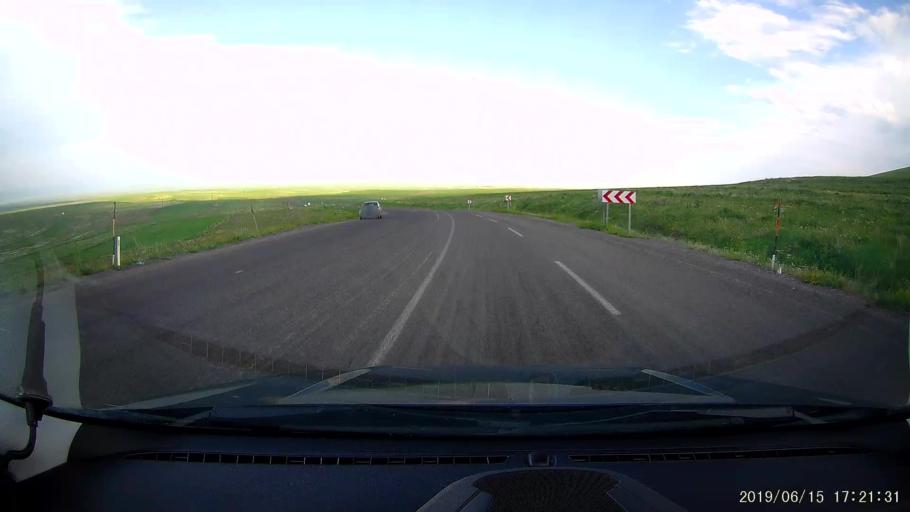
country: TR
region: Kars
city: Basgedikler
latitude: 40.6171
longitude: 43.3262
